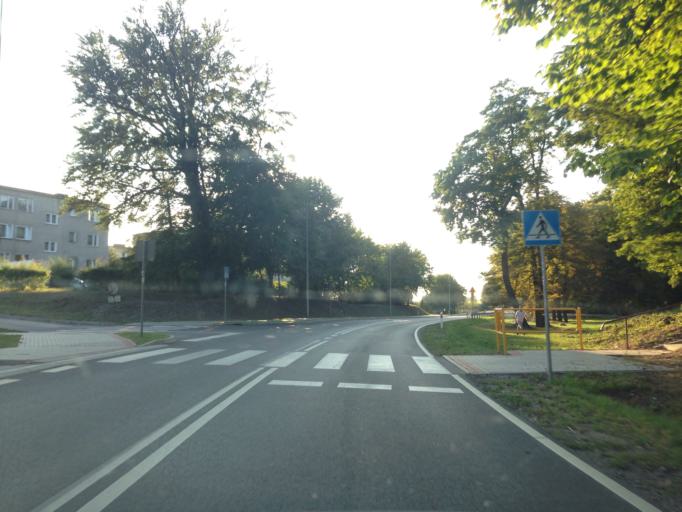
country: PL
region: Warmian-Masurian Voivodeship
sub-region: Powiat ilawski
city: Susz
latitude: 53.6979
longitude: 19.3842
